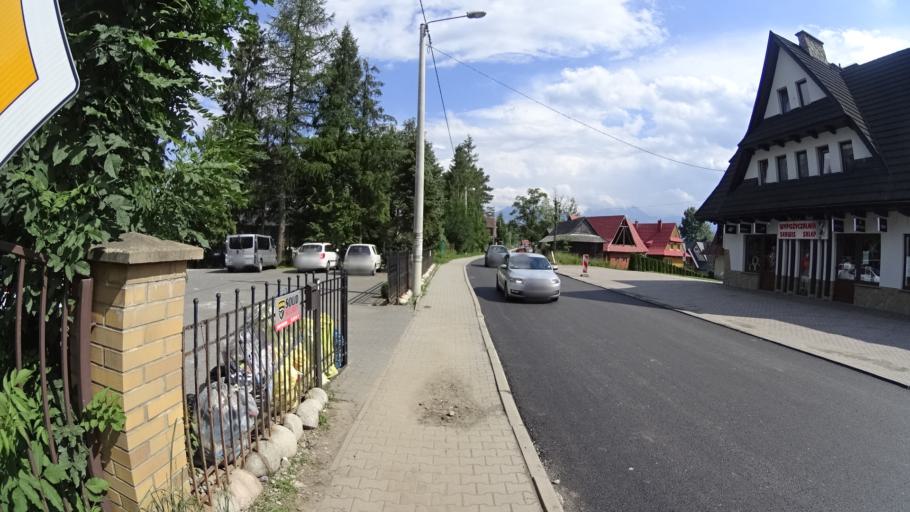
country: PL
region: Lesser Poland Voivodeship
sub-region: Powiat tatrzanski
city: Bukowina Tatrzanska
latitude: 49.3327
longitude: 20.0929
